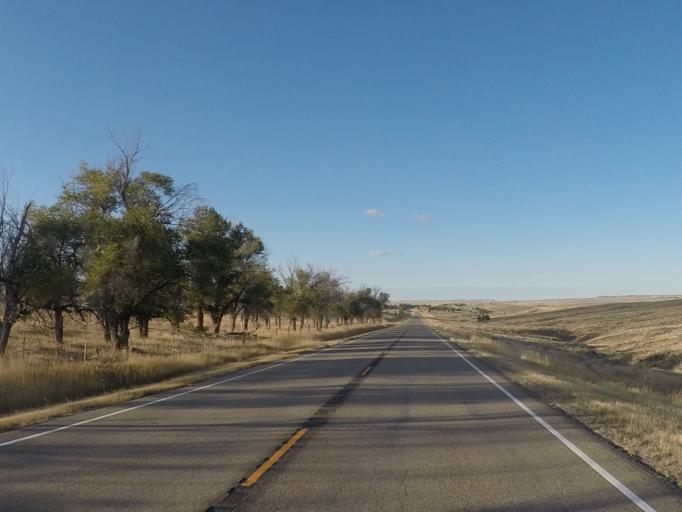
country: US
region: Montana
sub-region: Golden Valley County
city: Ryegate
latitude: 46.2458
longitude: -108.9364
